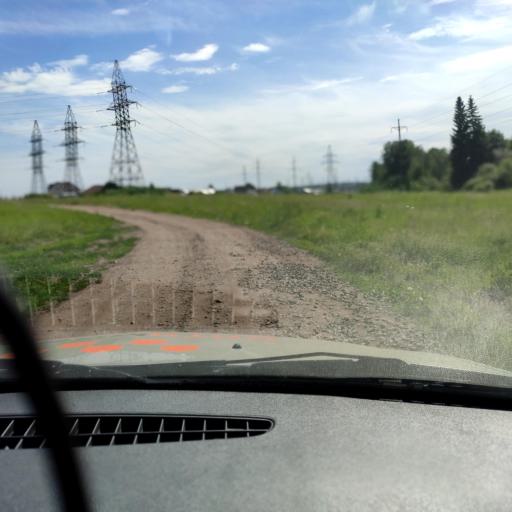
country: RU
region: Bashkortostan
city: Ufa
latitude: 54.6828
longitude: 56.0866
